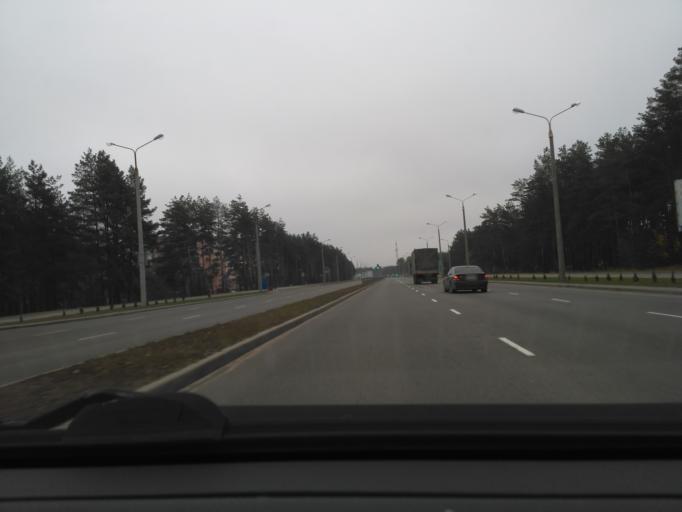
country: BY
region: Minsk
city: Horad Barysaw
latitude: 54.1987
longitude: 28.4746
